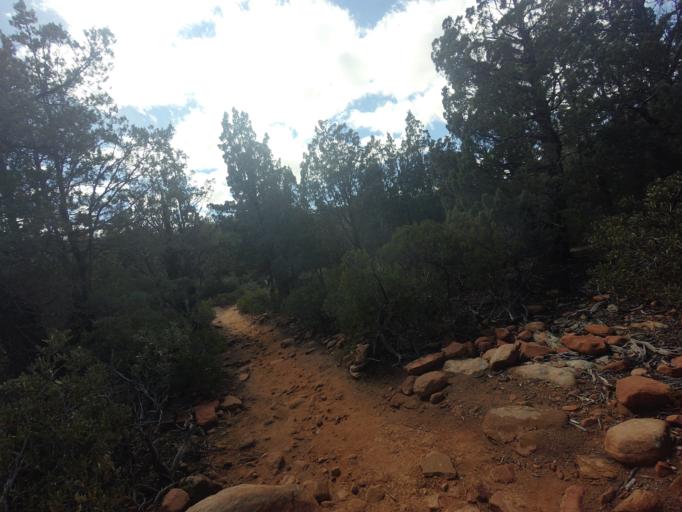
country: US
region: Arizona
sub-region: Yavapai County
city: West Sedona
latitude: 34.8953
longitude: -111.8203
